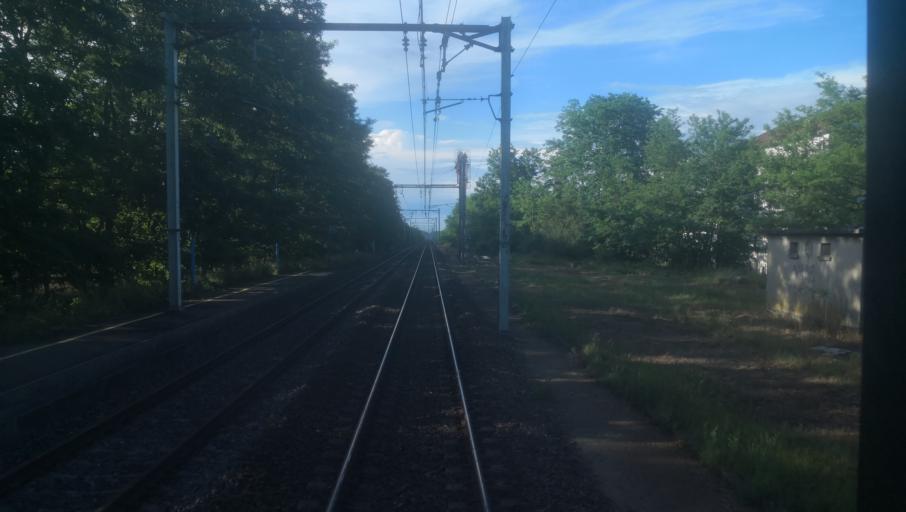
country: FR
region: Centre
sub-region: Departement du Loir-et-Cher
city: Theillay
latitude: 47.3169
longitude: 2.0447
